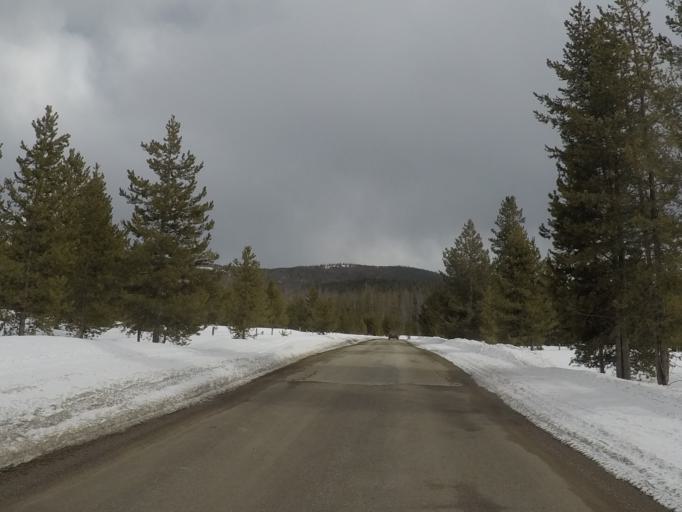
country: US
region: Montana
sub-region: Granite County
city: Philipsburg
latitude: 46.2099
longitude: -113.2530
